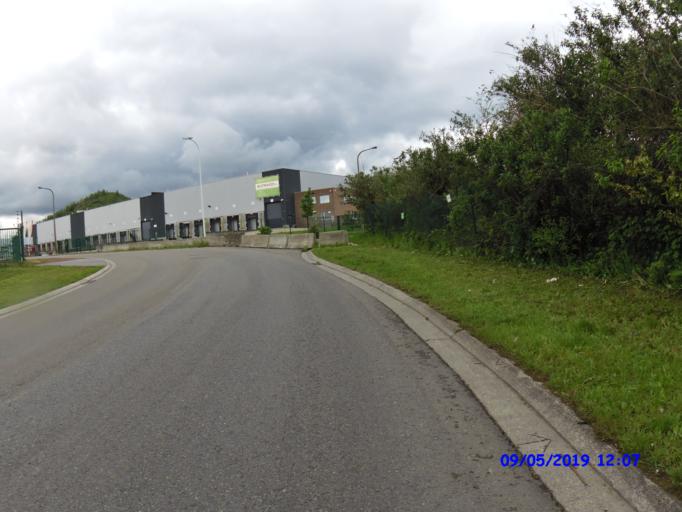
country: BE
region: Wallonia
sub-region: Province du Hainaut
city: Chatelet
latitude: 50.4018
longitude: 4.4986
